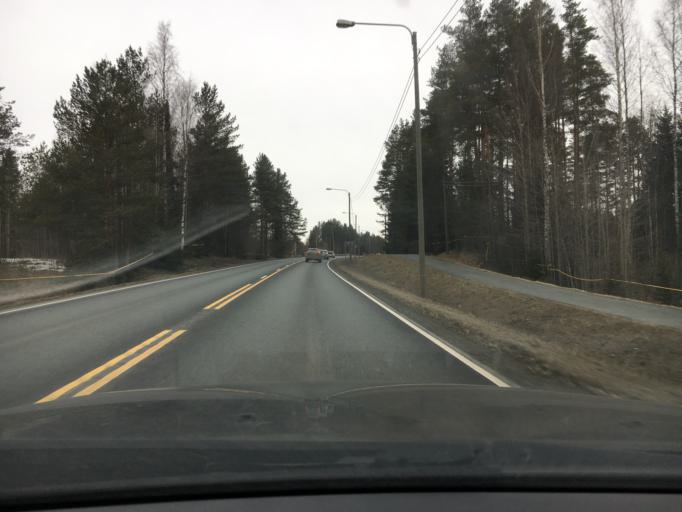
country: FI
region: Northern Savo
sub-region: Kuopio
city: Siilinjaervi
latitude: 63.1176
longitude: 27.6373
